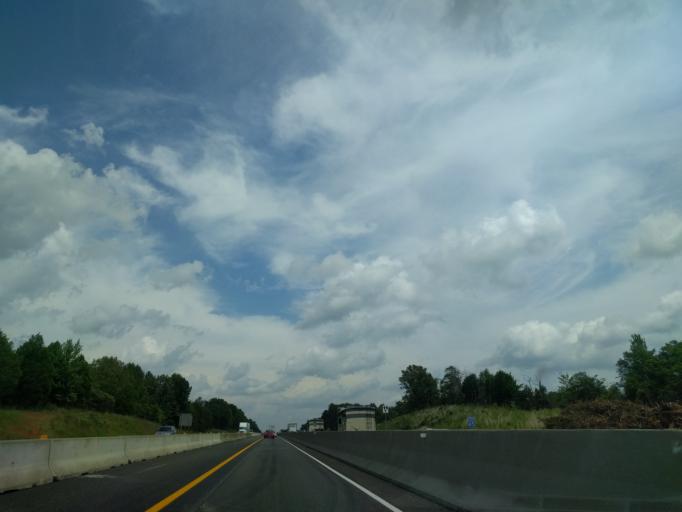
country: US
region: Kentucky
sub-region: Hardin County
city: Elizabethtown
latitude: 37.6015
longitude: -85.8676
